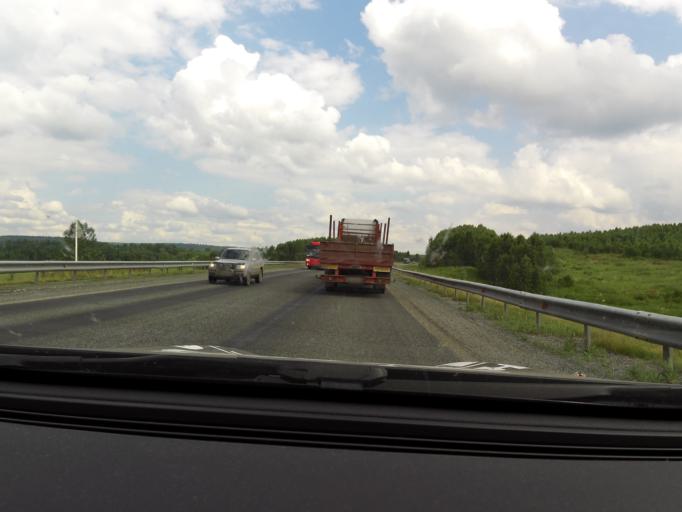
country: RU
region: Sverdlovsk
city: Ufimskiy
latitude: 56.7904
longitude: 58.3452
